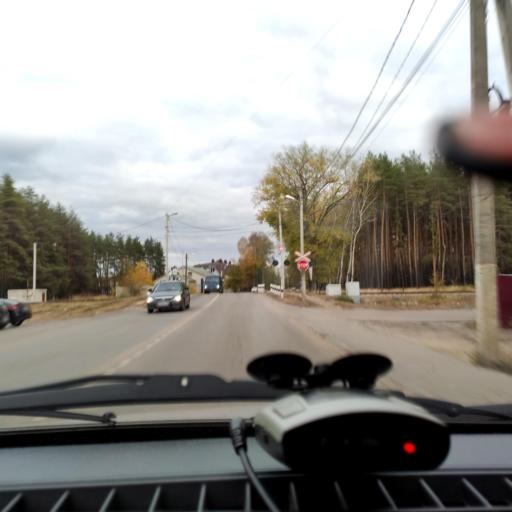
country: RU
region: Voronezj
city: Podgornoye
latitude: 51.7401
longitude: 39.1671
